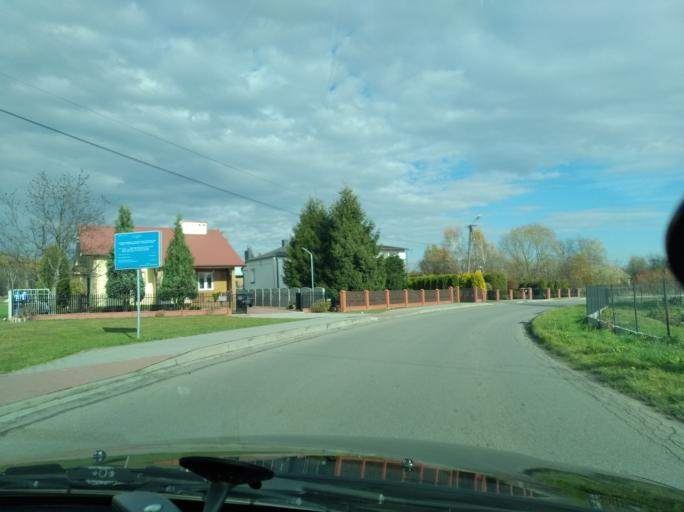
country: PL
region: Subcarpathian Voivodeship
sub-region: Powiat ropczycko-sedziszowski
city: Ostrow
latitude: 50.1005
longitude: 21.5980
